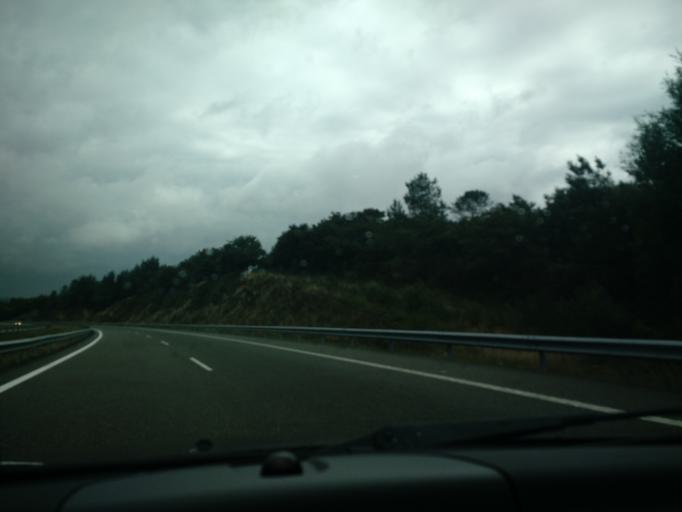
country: ES
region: Galicia
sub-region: Provincia da Coruna
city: Oroso
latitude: 42.9509
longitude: -8.4580
